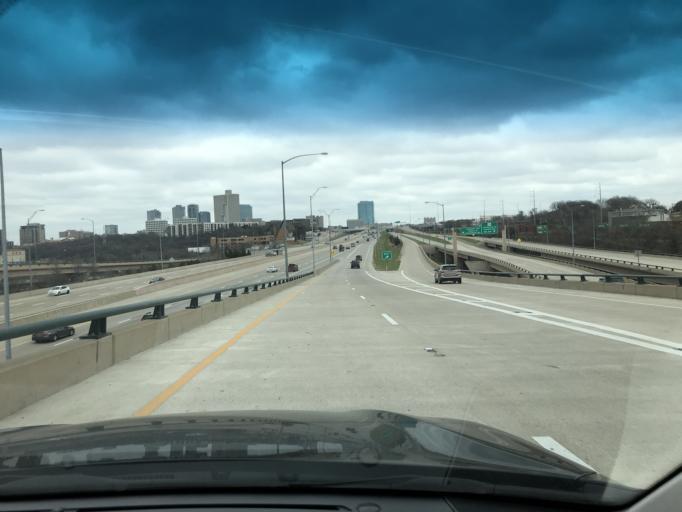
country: US
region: Texas
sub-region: Tarrant County
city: Fort Worth
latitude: 32.7384
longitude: -97.3505
